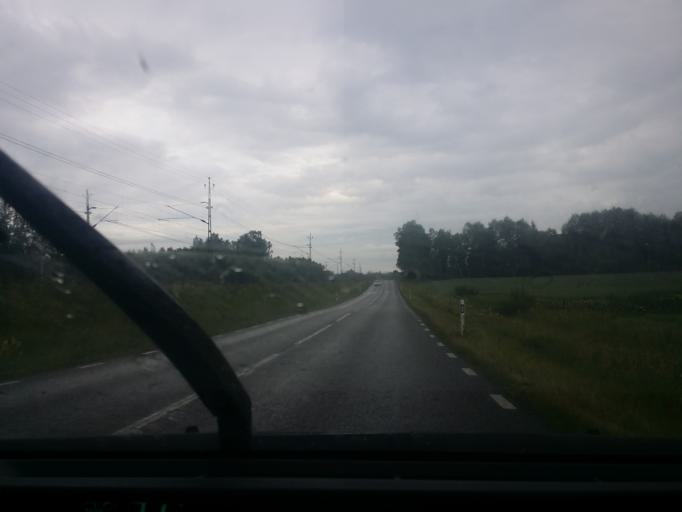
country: SE
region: OErebro
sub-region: Lindesbergs Kommun
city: Frovi
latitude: 59.4632
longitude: 15.3237
